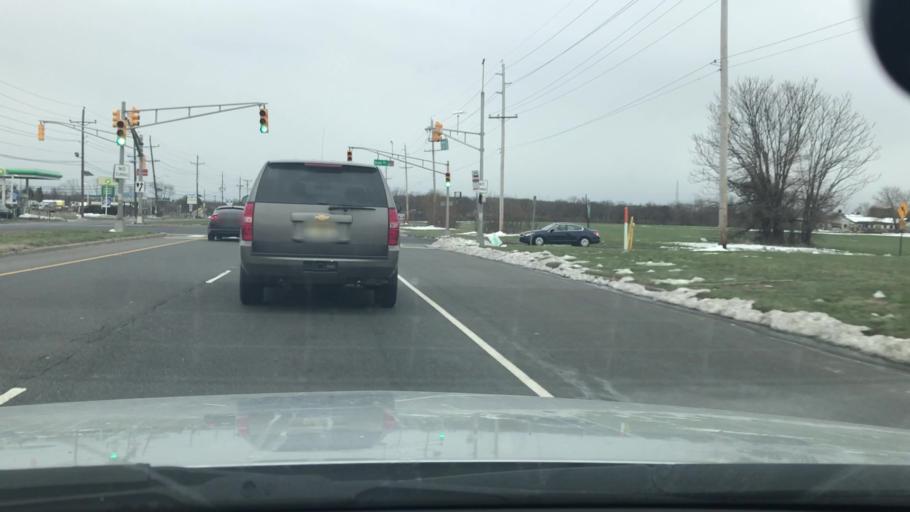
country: US
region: New Jersey
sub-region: Burlington County
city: Willingboro
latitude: 40.0323
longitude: -74.8223
